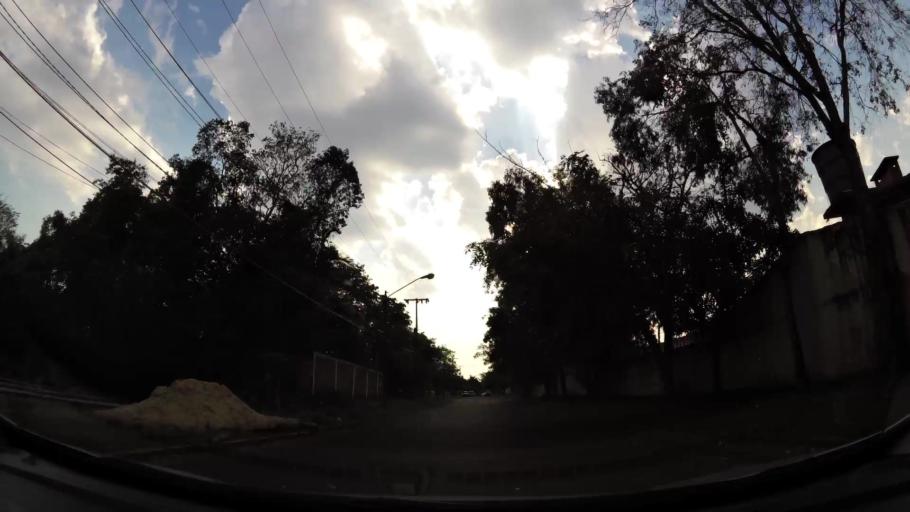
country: PY
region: Alto Parana
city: Presidente Franco
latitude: -25.5203
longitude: -54.6330
